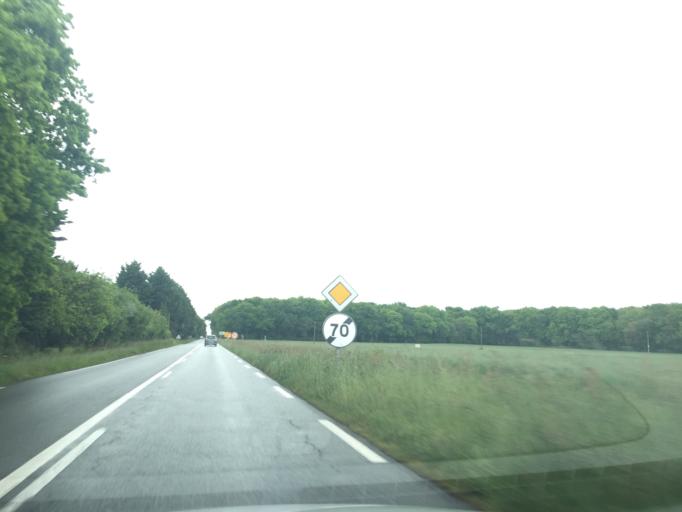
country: FR
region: Brittany
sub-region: Departement des Cotes-d'Armor
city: Ploubalay
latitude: 48.5942
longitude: -2.0993
